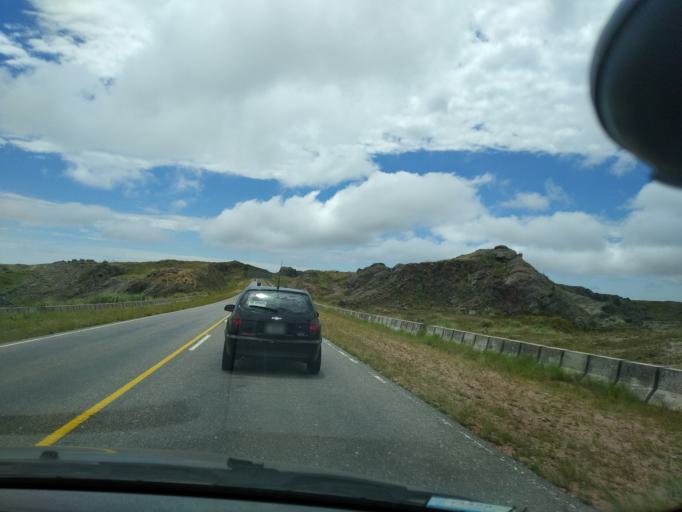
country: AR
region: Cordoba
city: Cuesta Blanca
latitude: -31.6087
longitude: -64.7357
